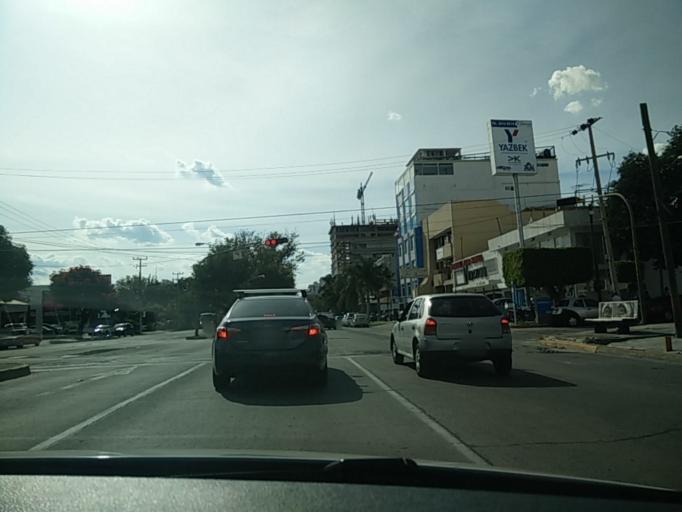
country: MX
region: Jalisco
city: Guadalajara
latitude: 20.6795
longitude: -103.3798
